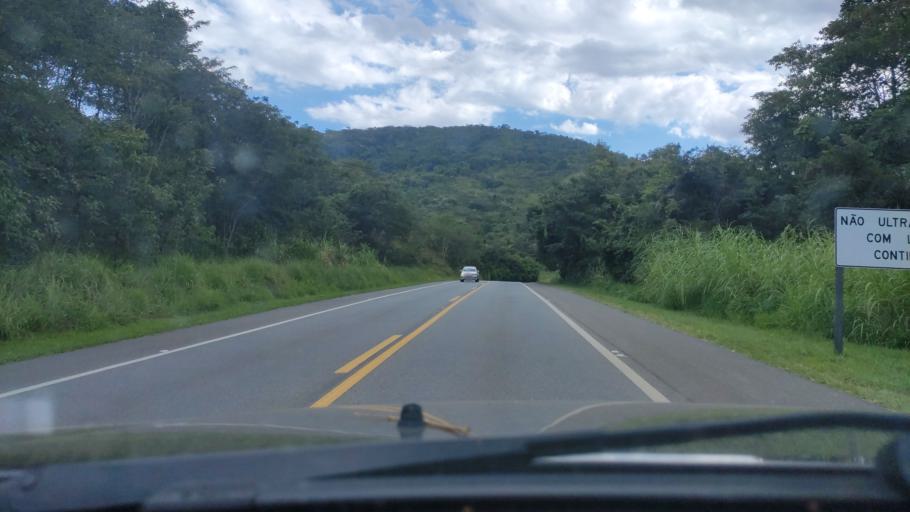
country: BR
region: Sao Paulo
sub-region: Aguas De Lindoia
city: Aguas de Lindoia
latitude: -22.4710
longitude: -46.7080
